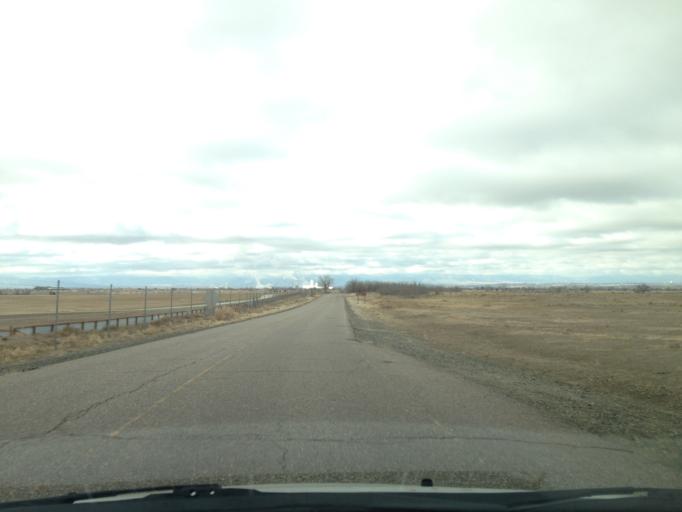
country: US
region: Colorado
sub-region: Adams County
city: Derby
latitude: 39.8130
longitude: -104.8777
